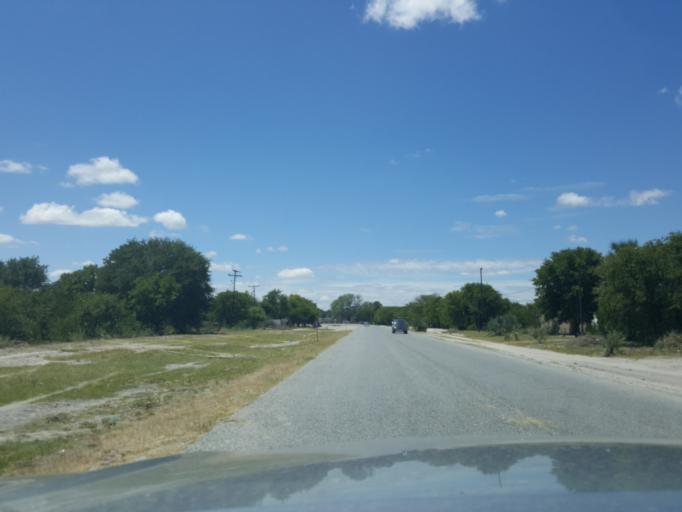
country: BW
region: Central
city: Nata
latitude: -20.2123
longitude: 26.1760
